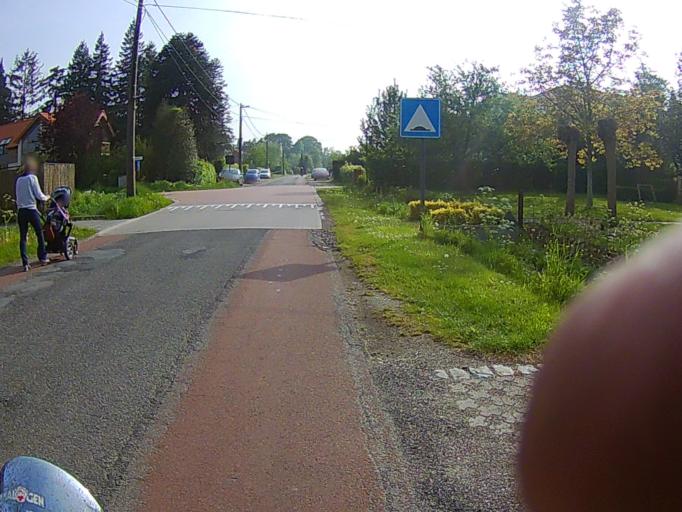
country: BE
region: Flanders
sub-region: Provincie Antwerpen
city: Ranst
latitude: 51.1979
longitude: 4.5461
